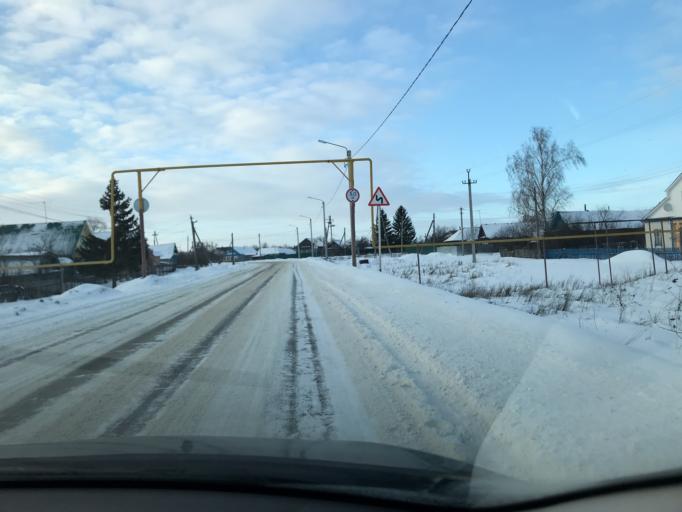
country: RU
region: Ulyanovsk
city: Undory
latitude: 54.6050
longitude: 48.4065
